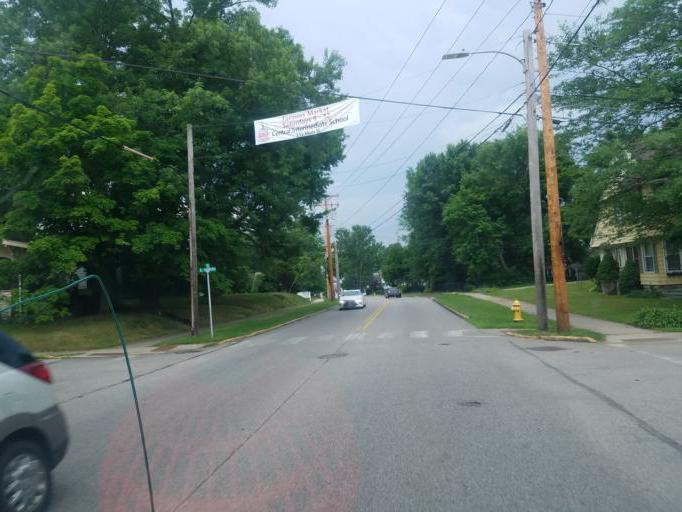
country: US
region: Ohio
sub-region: Medina County
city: Wadsworth
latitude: 41.0324
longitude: -81.7296
